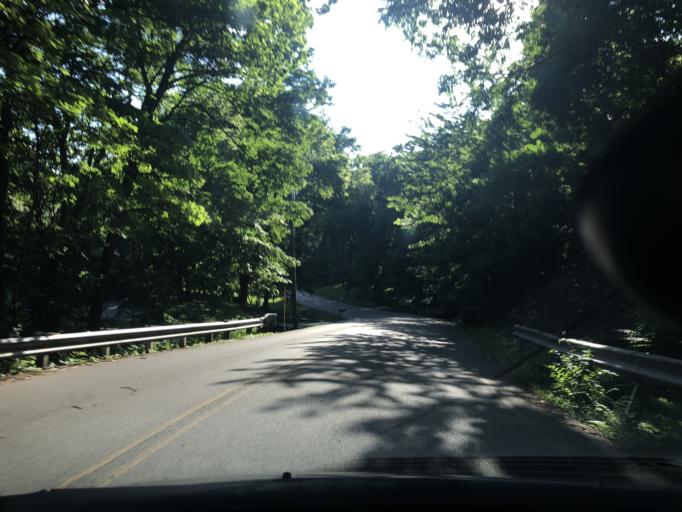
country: US
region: Tennessee
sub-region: Davidson County
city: Forest Hills
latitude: 36.0737
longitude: -86.8174
